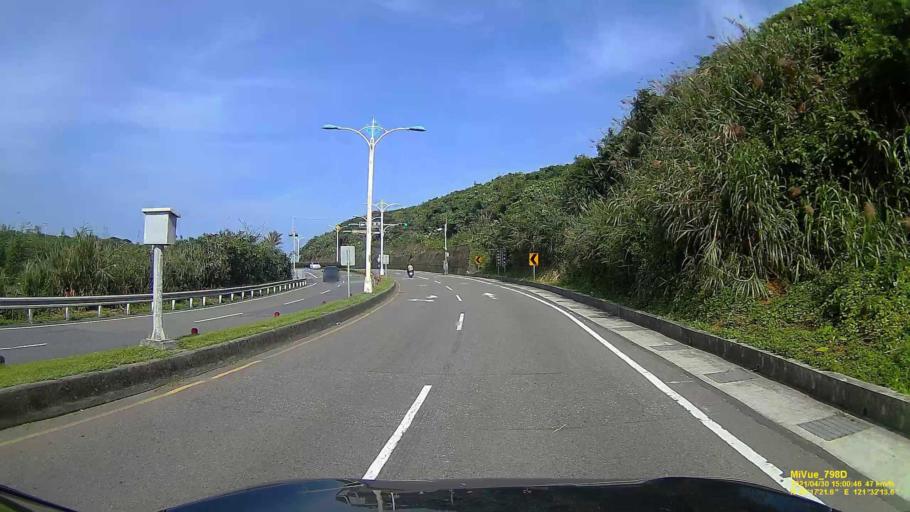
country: TW
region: Taipei
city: Taipei
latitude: 25.2893
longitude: 121.5373
